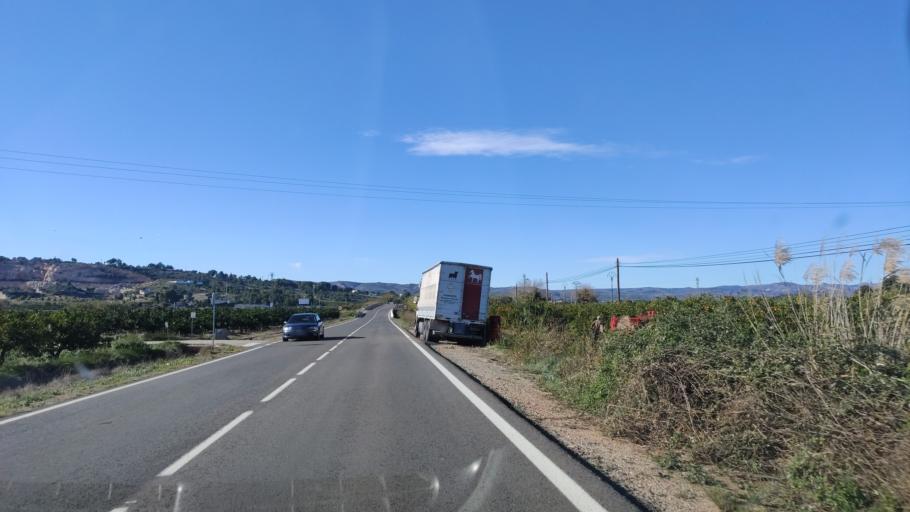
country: ES
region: Valencia
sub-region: Provincia de Valencia
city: Alberic
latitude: 39.1214
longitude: -0.5427
